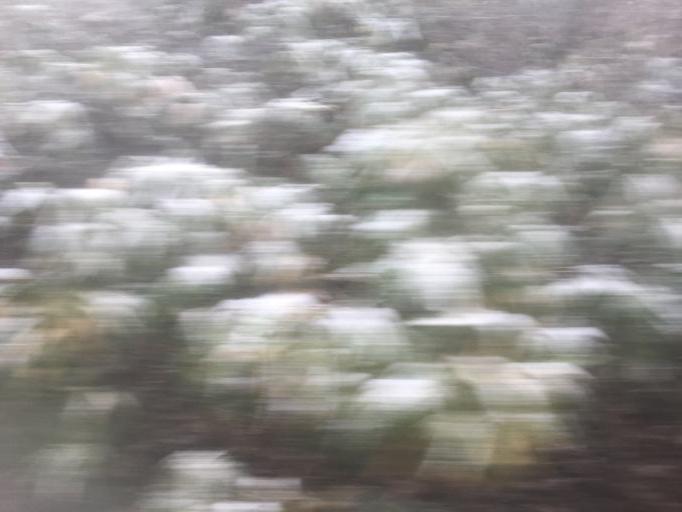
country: JP
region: Aomori
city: Goshogawara
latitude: 41.1029
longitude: 140.5280
